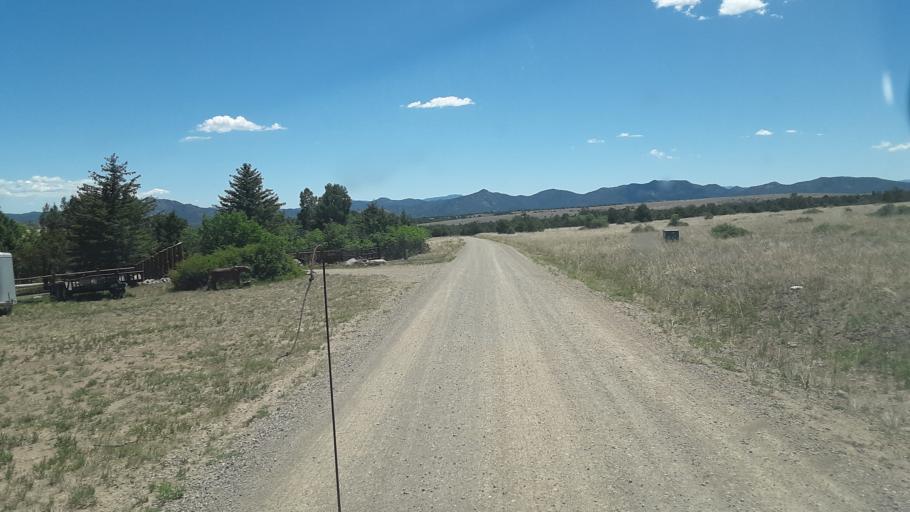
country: US
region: Colorado
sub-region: Custer County
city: Westcliffe
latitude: 38.3053
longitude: -105.6762
